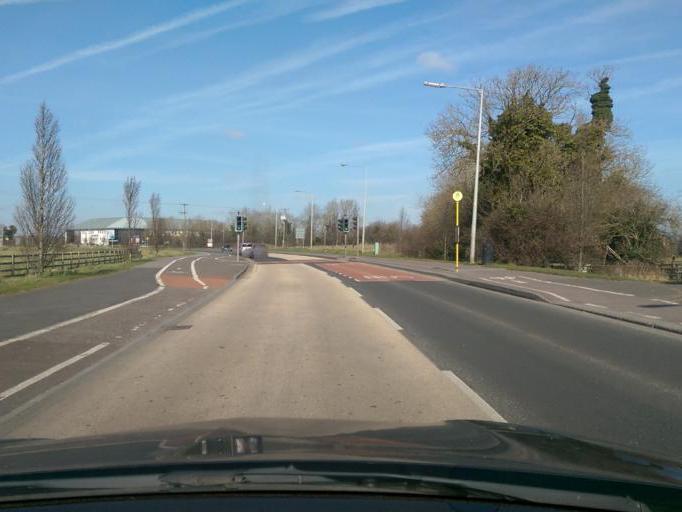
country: IE
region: Leinster
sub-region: Kildare
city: Celbridge
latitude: 53.3552
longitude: -6.5470
